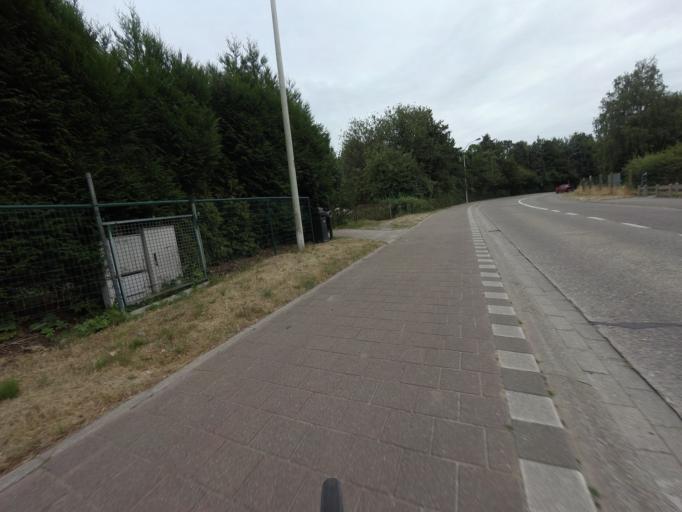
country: BE
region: Flanders
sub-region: Provincie Antwerpen
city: Schoten
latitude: 51.2509
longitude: 4.5077
